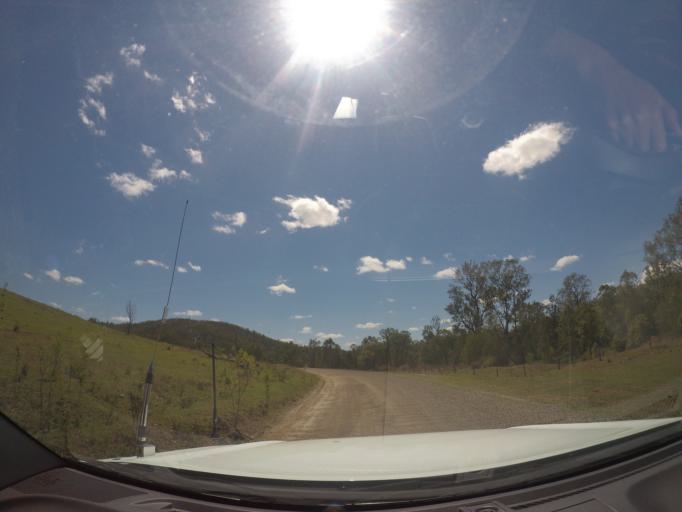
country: AU
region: Queensland
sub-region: Logan
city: Cedar Vale
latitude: -27.8633
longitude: 152.8538
